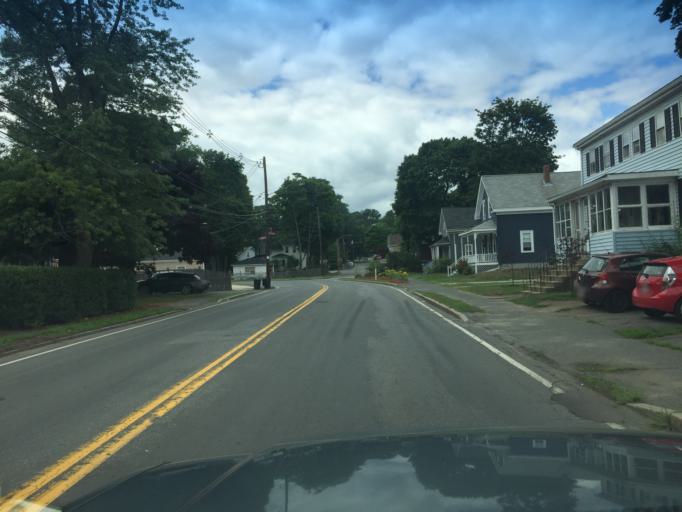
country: US
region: Massachusetts
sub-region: Middlesex County
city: Reading
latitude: 42.5211
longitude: -71.0968
